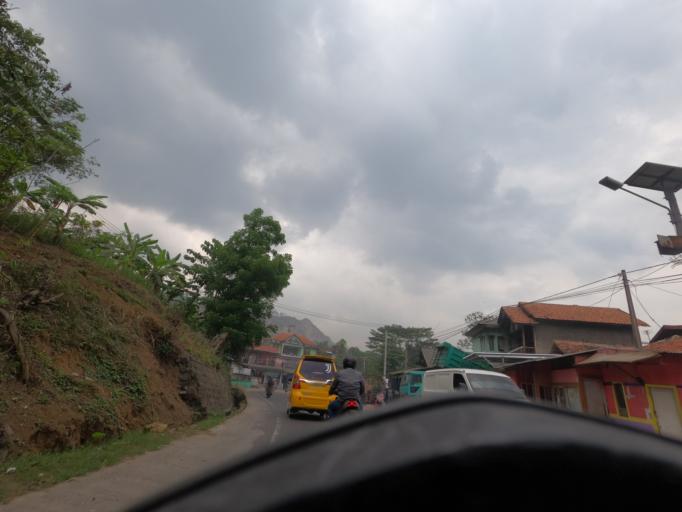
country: ID
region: West Java
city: Padalarang
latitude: -6.8313
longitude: 107.4406
